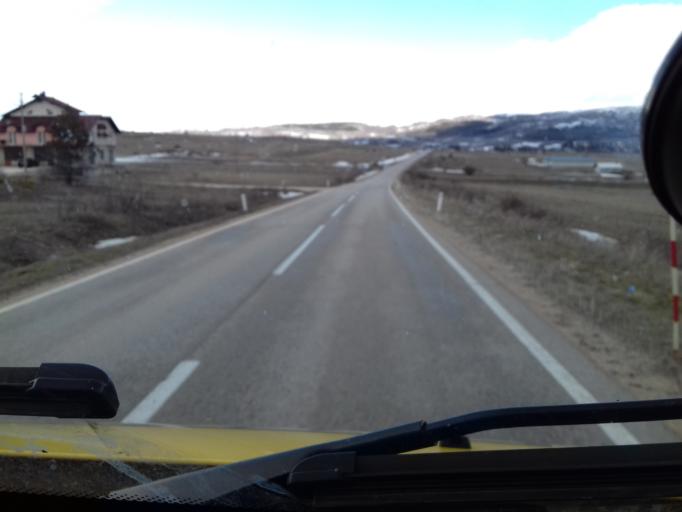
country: BA
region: Federation of Bosnia and Herzegovina
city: Tomislavgrad
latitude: 43.7400
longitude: 17.2245
